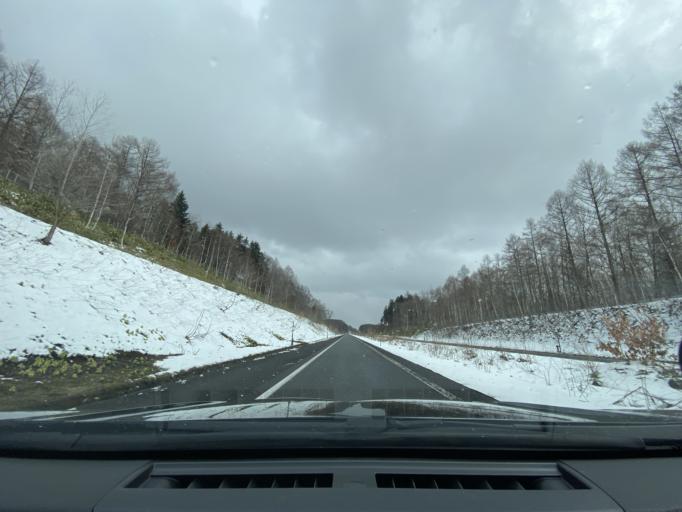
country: JP
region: Hokkaido
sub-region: Asahikawa-shi
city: Asahikawa
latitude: 43.9750
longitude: 142.4613
